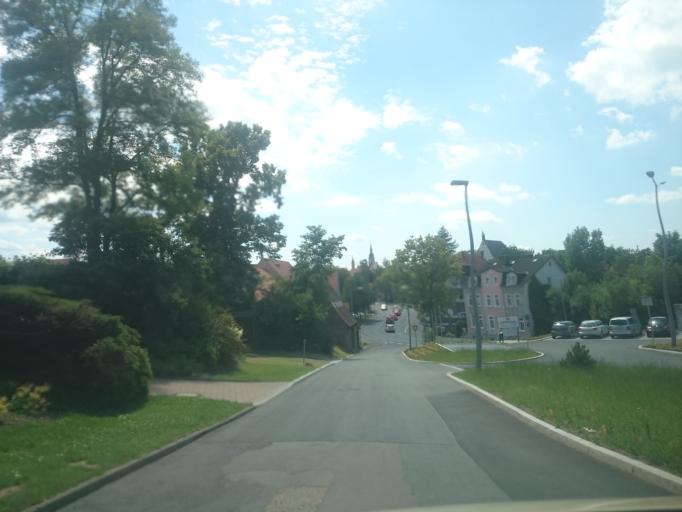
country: DE
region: Saxony
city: Freiberg
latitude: 50.9230
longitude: 13.3499
